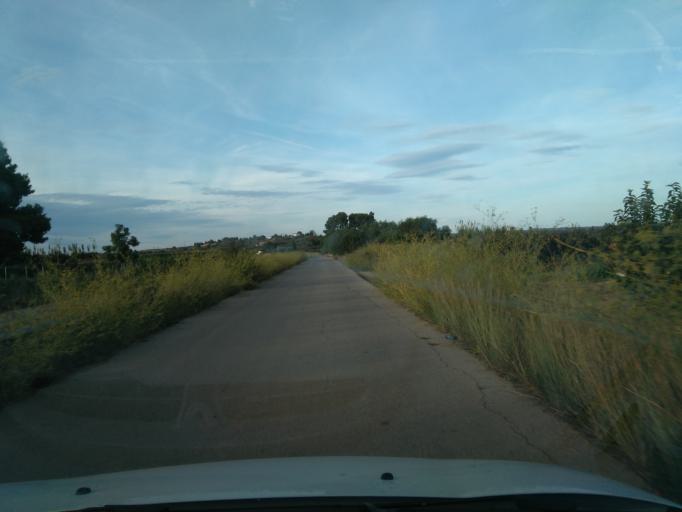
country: ES
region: Valencia
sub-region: Provincia de Valencia
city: Benimodo
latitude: 39.1968
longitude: -0.5667
